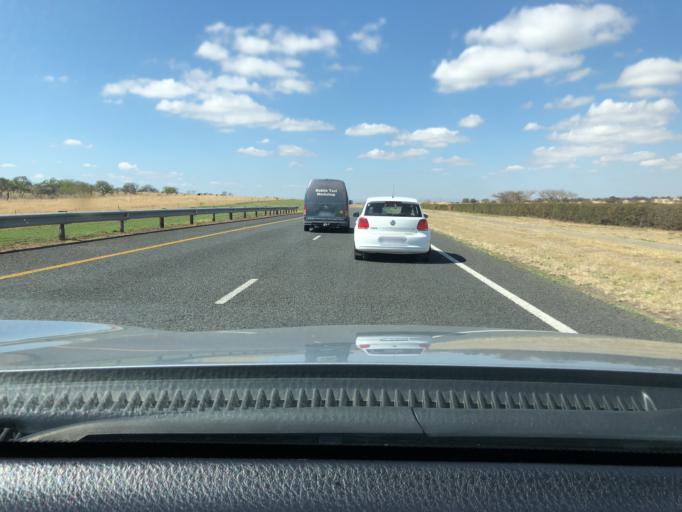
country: ZA
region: KwaZulu-Natal
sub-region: uThukela District Municipality
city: Estcourt
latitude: -28.8378
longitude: 29.7112
